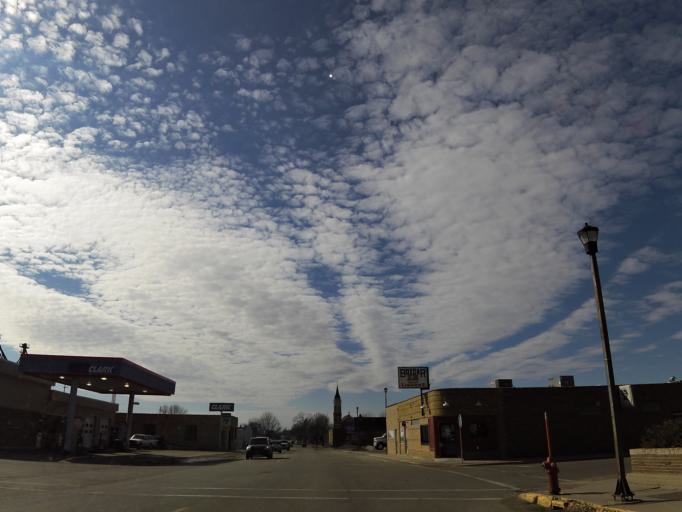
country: US
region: Minnesota
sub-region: Waseca County
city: Waseca
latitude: 44.0777
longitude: -93.5085
